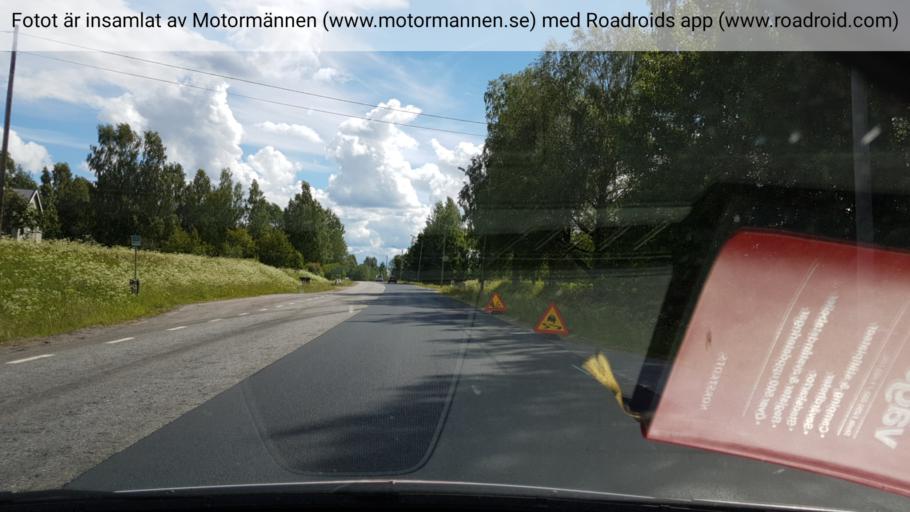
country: SE
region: Vaesternorrland
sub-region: Solleftea Kommun
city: Solleftea
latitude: 63.2405
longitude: 17.2070
